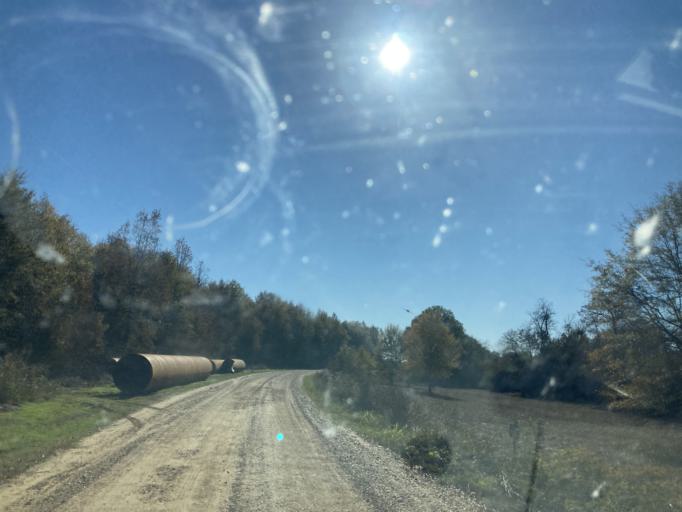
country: US
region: Mississippi
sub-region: Sharkey County
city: Rolling Fork
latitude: 32.7580
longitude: -90.6886
